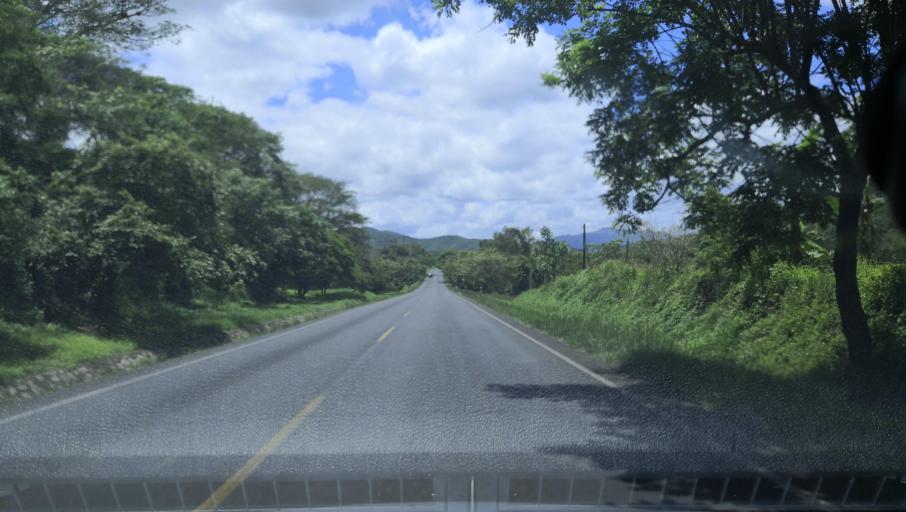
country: NI
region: Esteli
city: Condega
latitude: 13.2309
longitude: -86.3780
